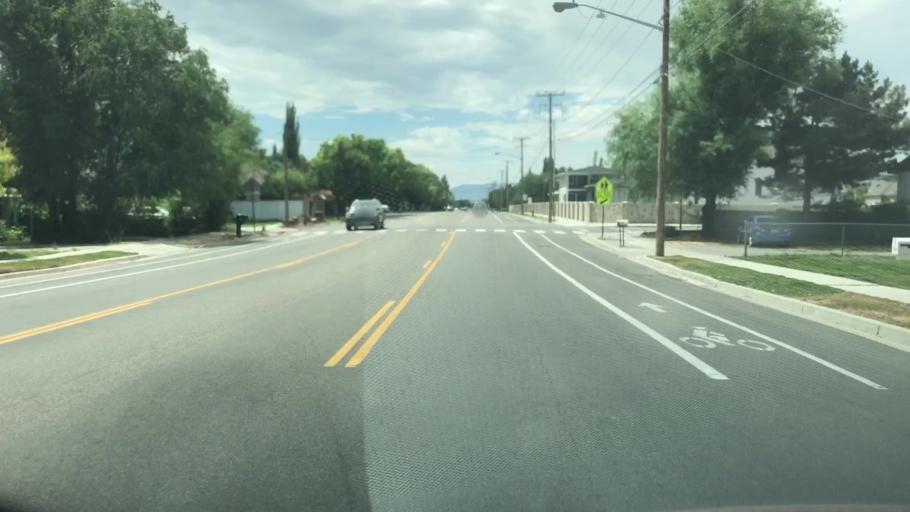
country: US
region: Utah
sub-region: Salt Lake County
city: South Jordan
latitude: 40.5489
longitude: -111.9292
